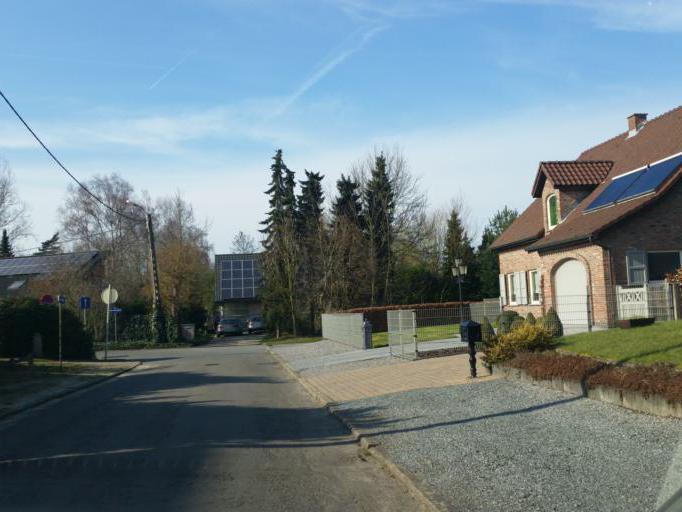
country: BE
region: Flanders
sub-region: Provincie Vlaams-Brabant
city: Boortmeerbeek
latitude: 50.9830
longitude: 4.5770
